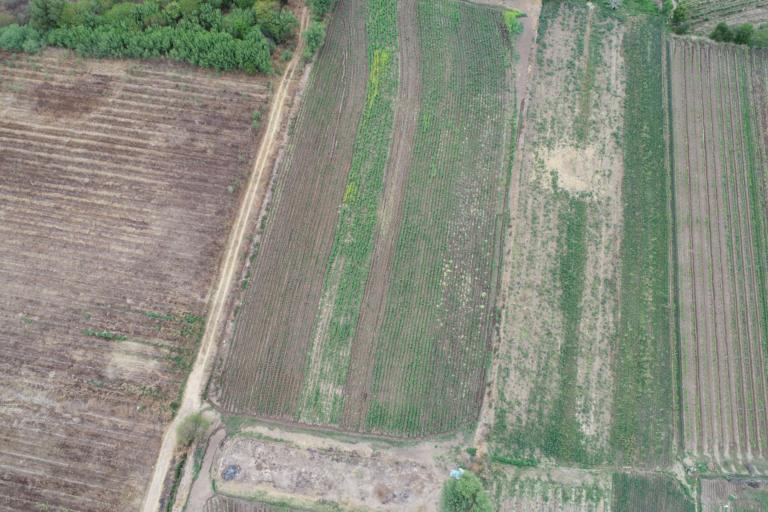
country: BO
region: Tarija
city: Tarija
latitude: -21.5981
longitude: -64.6155
